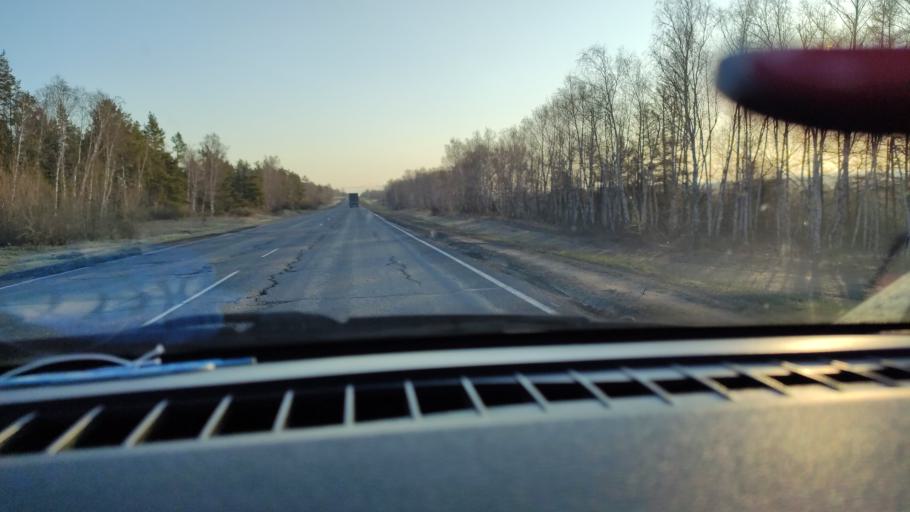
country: RU
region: Saratov
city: Sennoy
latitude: 52.1045
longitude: 46.8195
